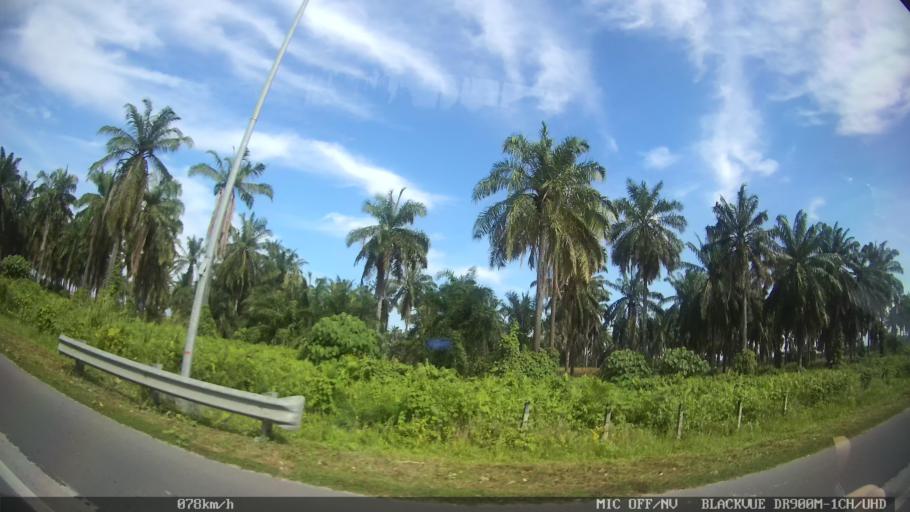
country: ID
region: North Sumatra
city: Medan
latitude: 3.6317
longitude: 98.6341
